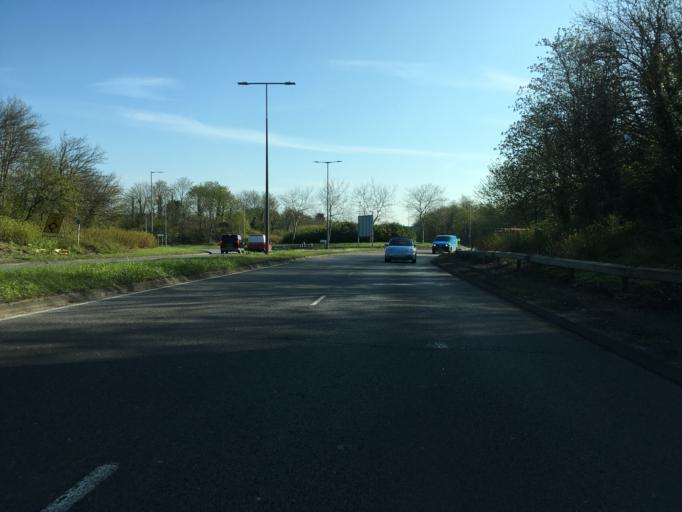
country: GB
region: England
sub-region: Milton Keynes
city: Milton Keynes
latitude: 52.0461
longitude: -0.7593
